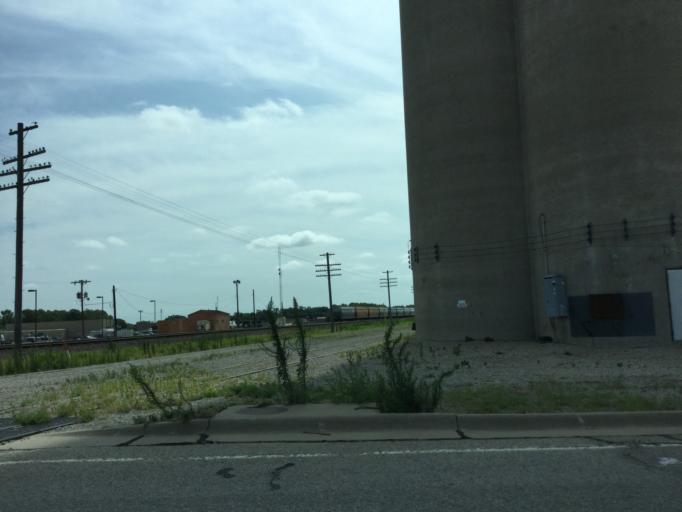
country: US
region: Kansas
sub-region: Shawnee County
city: Topeka
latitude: 39.0835
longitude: -95.7251
